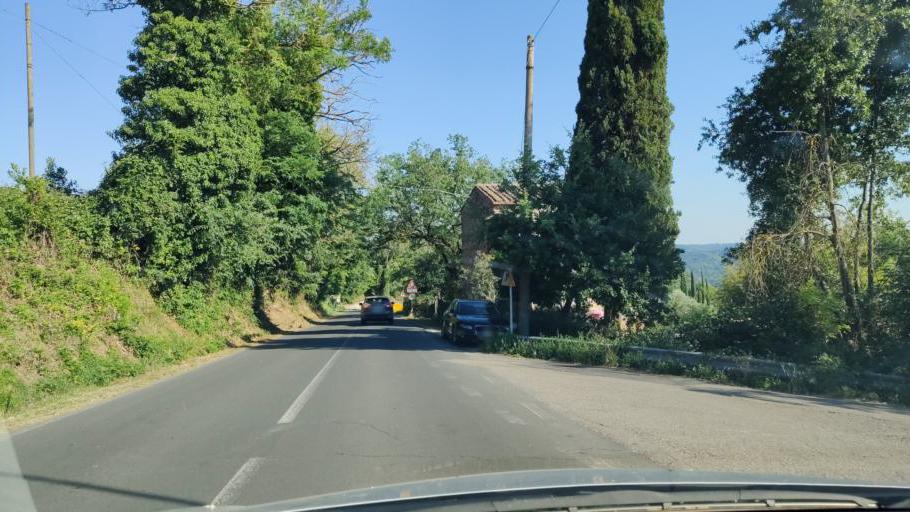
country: IT
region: Umbria
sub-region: Provincia di Terni
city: Penna in Teverina
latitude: 42.4906
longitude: 12.3530
